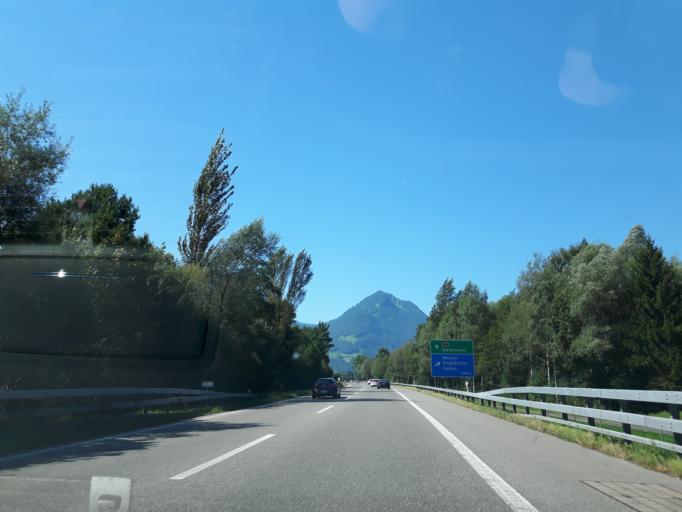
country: CH
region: Saint Gallen
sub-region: Wahlkreis See-Gaster
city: Weesen
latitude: 47.1269
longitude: 9.1073
